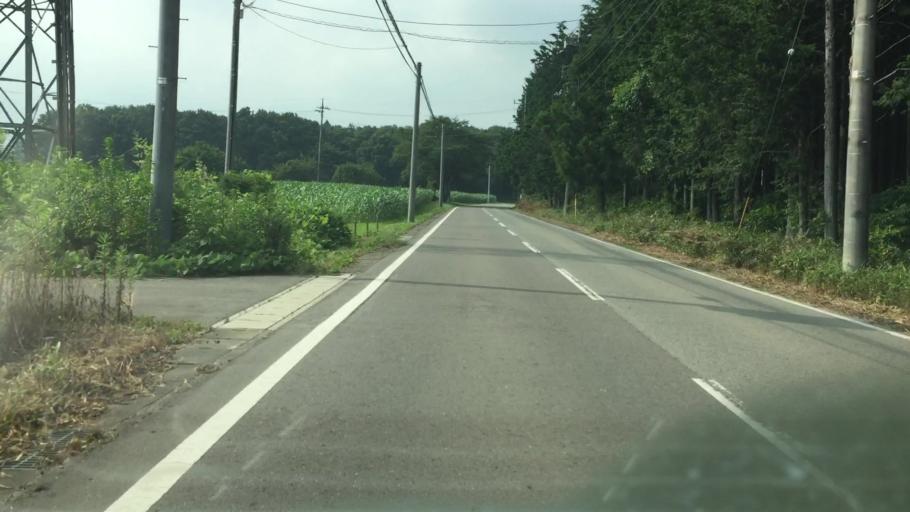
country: JP
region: Tochigi
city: Kuroiso
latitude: 36.9528
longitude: 139.9596
